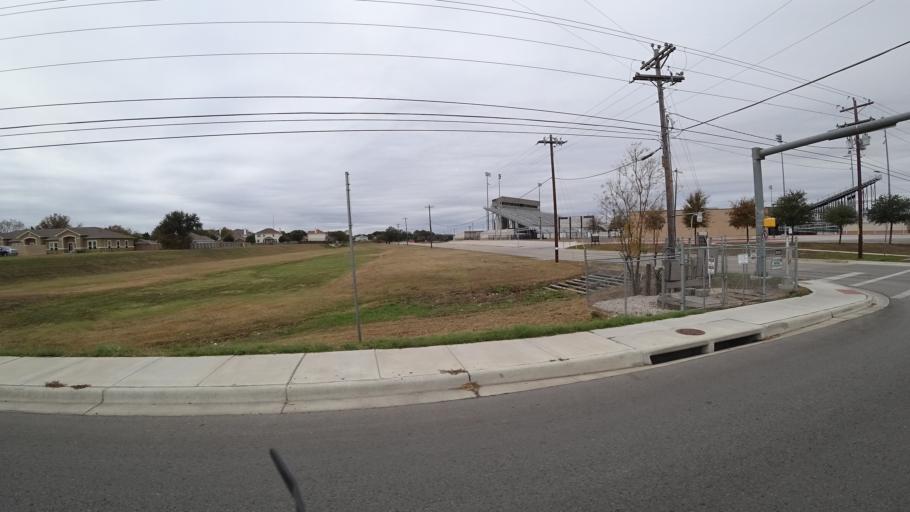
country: US
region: Texas
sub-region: Williamson County
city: Cedar Park
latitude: 30.5359
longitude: -97.8476
